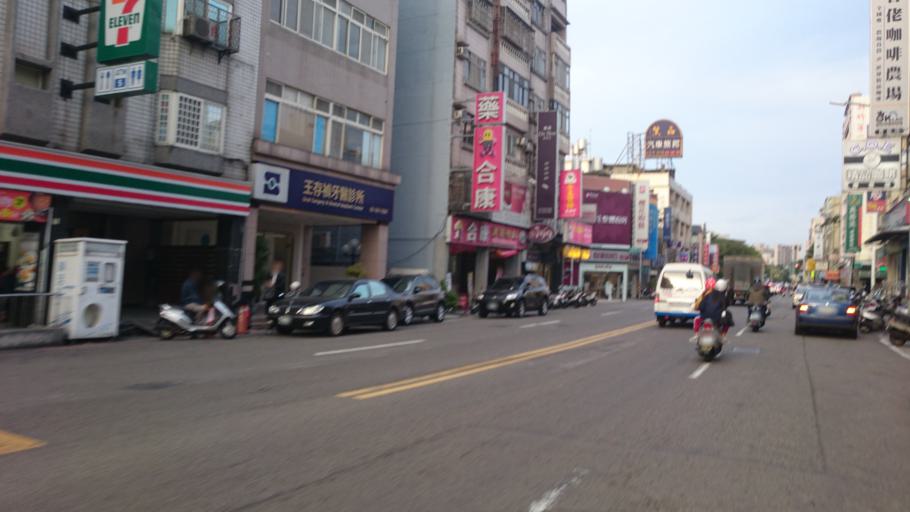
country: TW
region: Taiwan
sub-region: Hsinchu
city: Hsinchu
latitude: 24.7974
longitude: 120.9768
